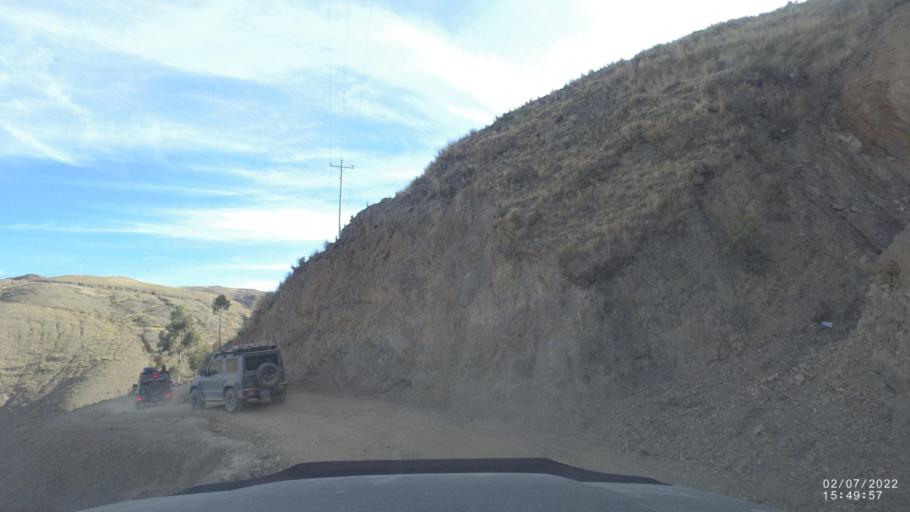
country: BO
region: Cochabamba
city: Irpa Irpa
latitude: -17.9029
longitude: -66.4116
